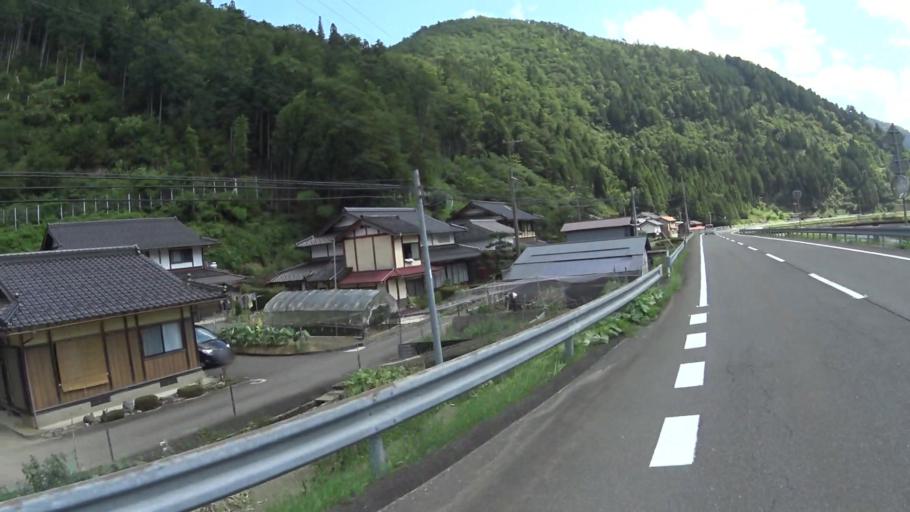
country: JP
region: Fukui
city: Obama
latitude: 35.3311
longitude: 135.5671
